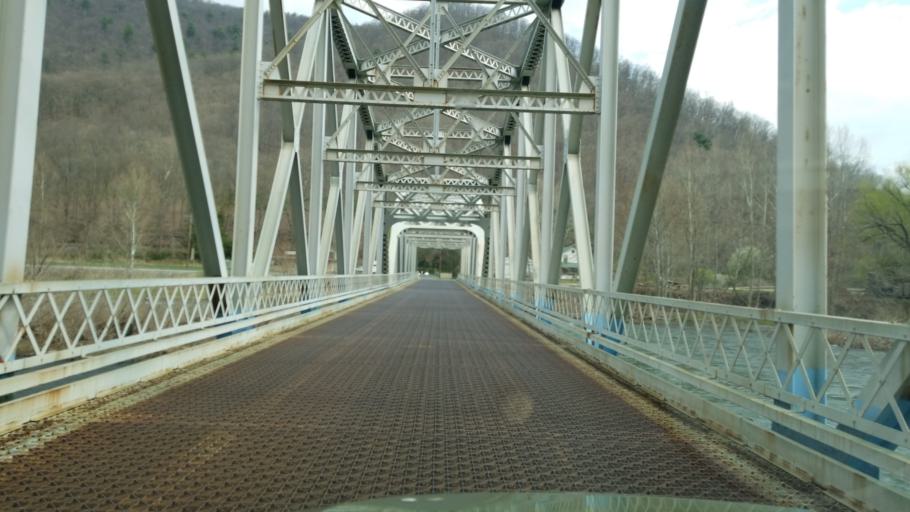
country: US
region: Pennsylvania
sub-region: Cameron County
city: Emporium
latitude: 41.3185
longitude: -78.0840
